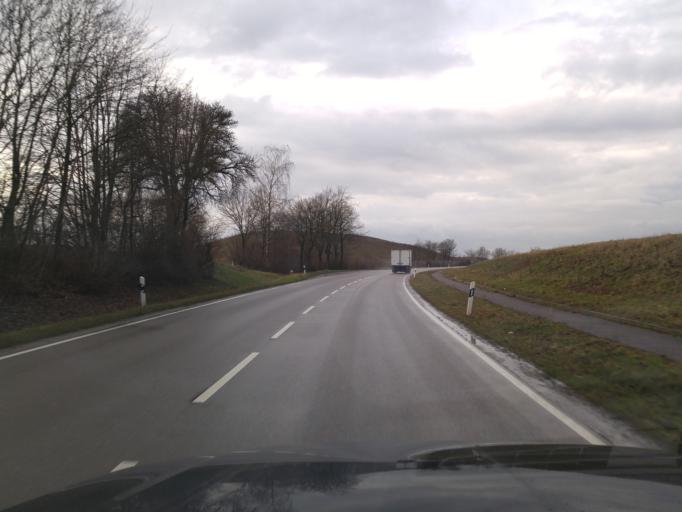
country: DE
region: Baden-Wuerttemberg
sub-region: Regierungsbezirk Stuttgart
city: Waldenburg
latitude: 49.2092
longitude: 9.6321
